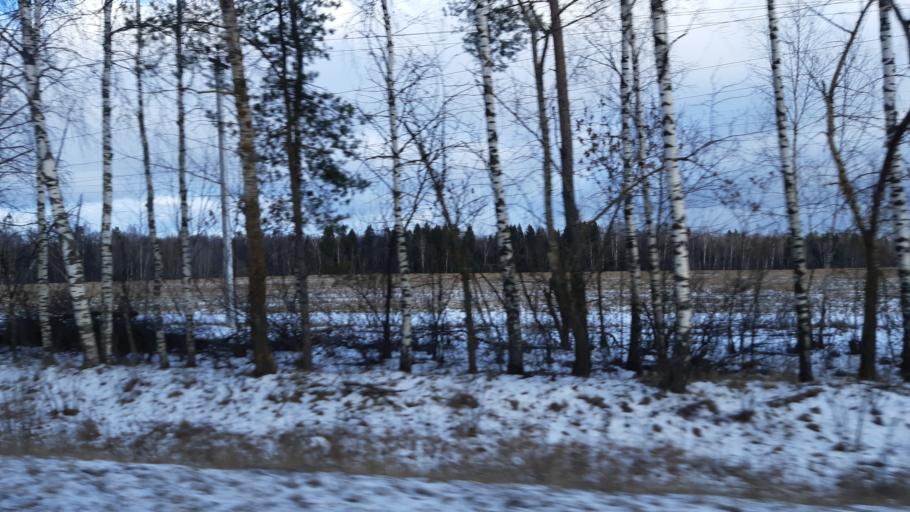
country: RU
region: Moskovskaya
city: Noginsk-9
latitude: 56.0320
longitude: 38.5547
